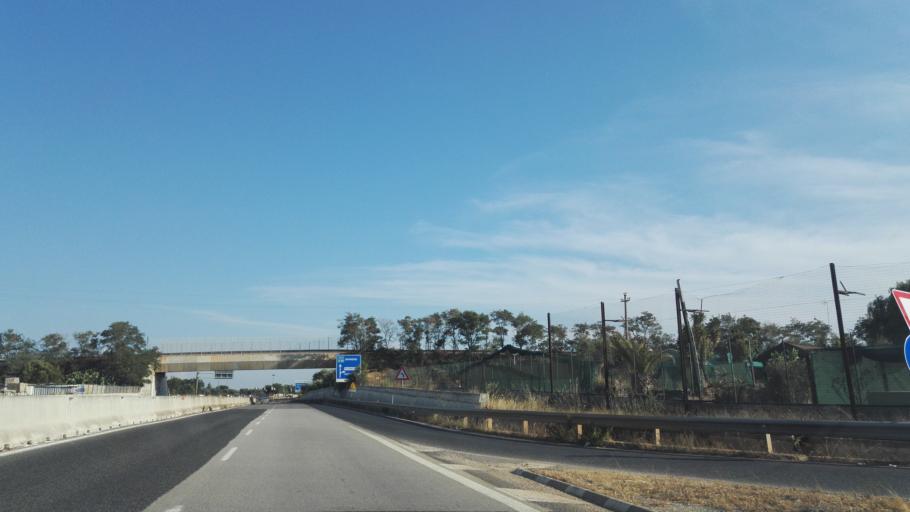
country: IT
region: Apulia
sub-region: Provincia di Bari
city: Polignano a Mare
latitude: 40.9921
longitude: 17.2067
